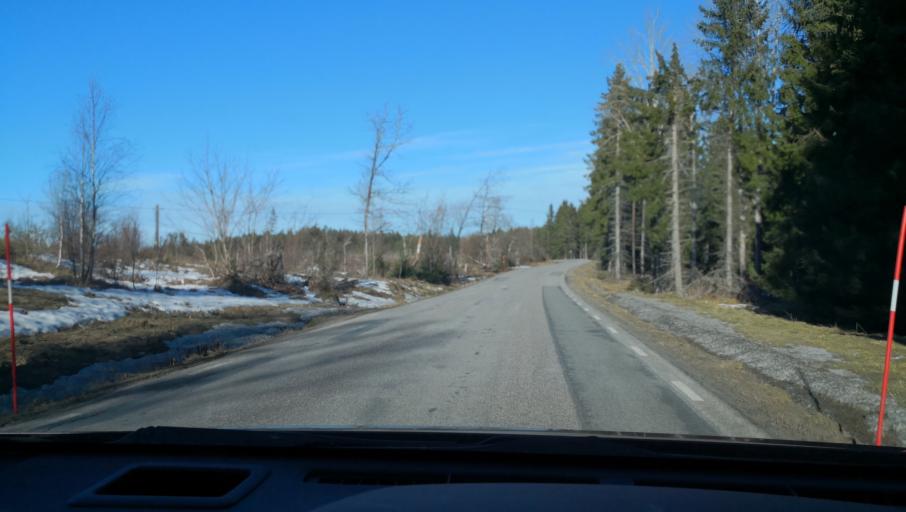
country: SE
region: Uppsala
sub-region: Osthammars Kommun
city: Osterbybruk
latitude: 60.2268
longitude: 17.9188
